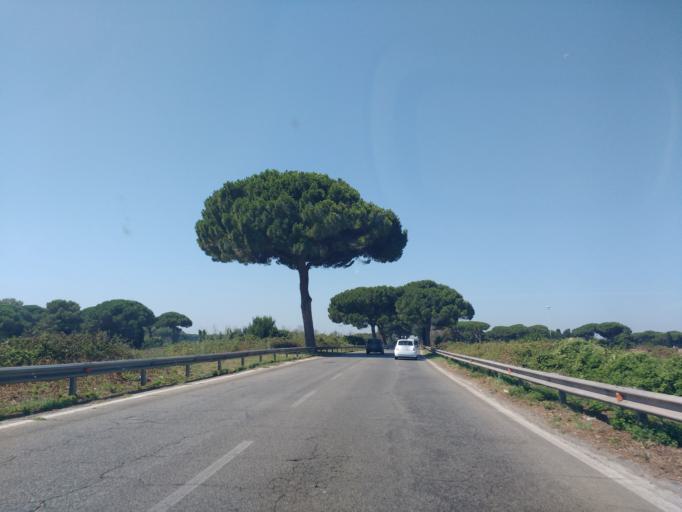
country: IT
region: Latium
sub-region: Citta metropolitana di Roma Capitale
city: Lido di Ostia
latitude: 41.7542
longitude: 12.2959
